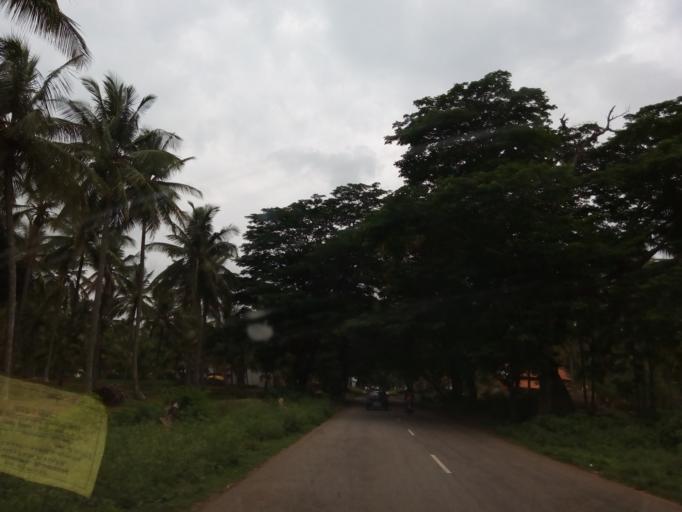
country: IN
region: Karnataka
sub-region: Hassan
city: Shravanabelagola
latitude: 12.8746
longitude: 76.4409
